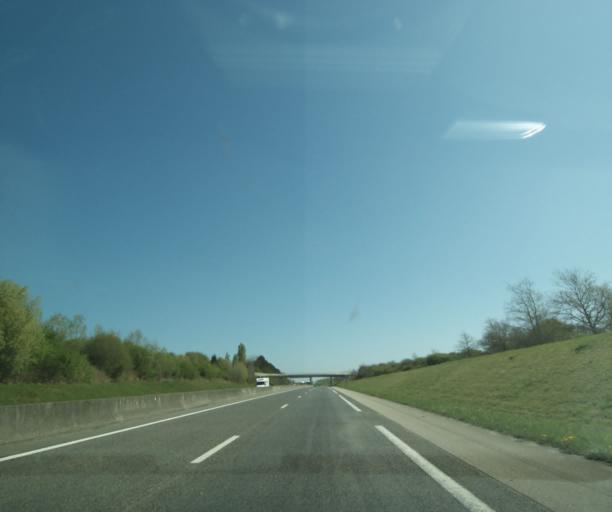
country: FR
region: Auvergne
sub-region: Departement de l'Allier
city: Toulon-sur-Allier
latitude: 46.5326
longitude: 3.3642
